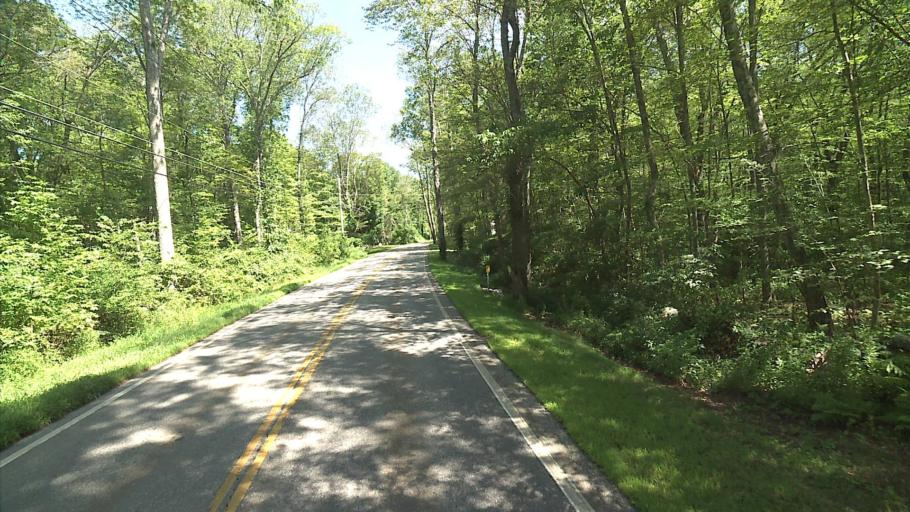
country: US
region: Connecticut
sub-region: Windham County
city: Windham
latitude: 41.7530
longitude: -72.0629
